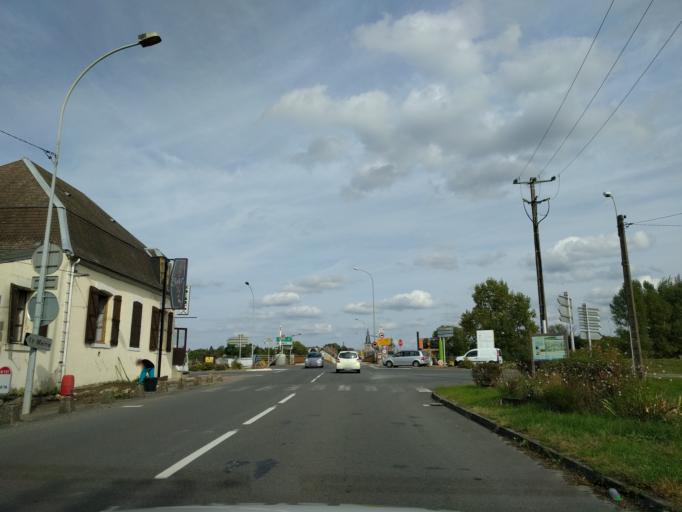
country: FR
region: Bourgogne
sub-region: Departement de la Nievre
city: La Charite-sur-Loire
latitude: 47.1744
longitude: 3.0077
